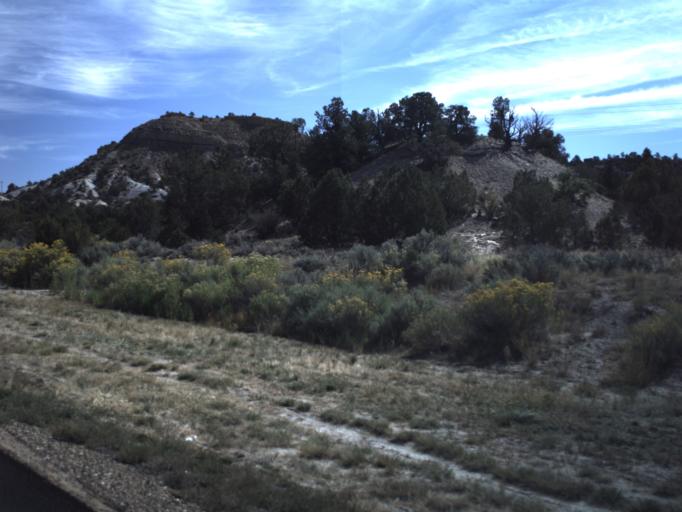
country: US
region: Utah
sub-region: Wayne County
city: Loa
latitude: 37.7725
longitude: -111.6503
